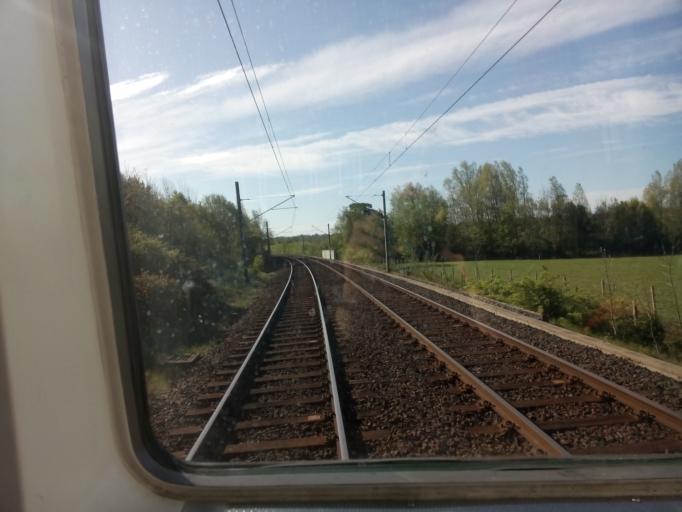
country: GB
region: England
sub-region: Newcastle upon Tyne
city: Dinnington
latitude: 55.0236
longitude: -1.6993
